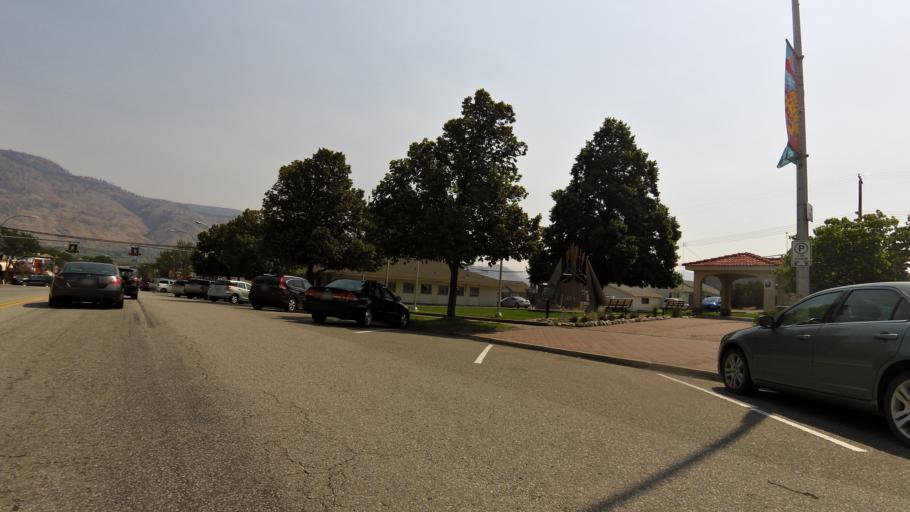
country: CA
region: British Columbia
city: Osoyoos
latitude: 49.0327
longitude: -119.4683
